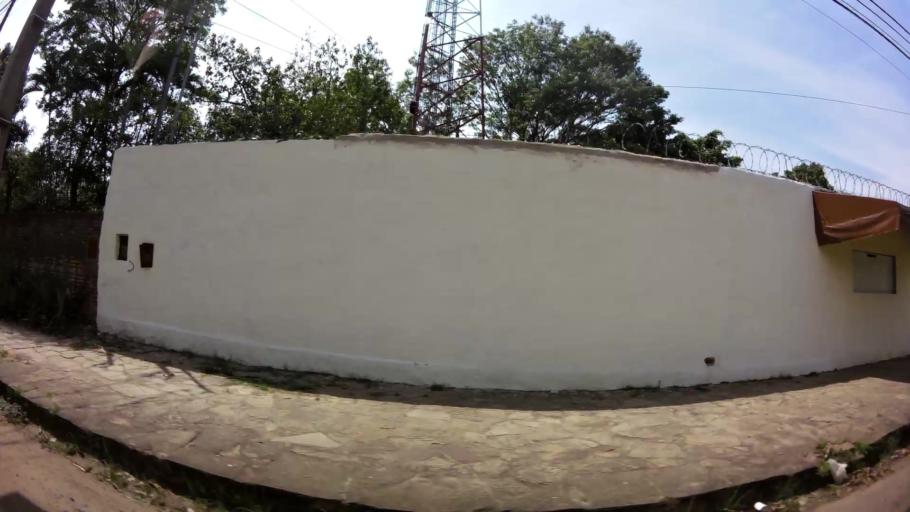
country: PY
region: Asuncion
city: Asuncion
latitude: -25.2804
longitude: -57.5898
